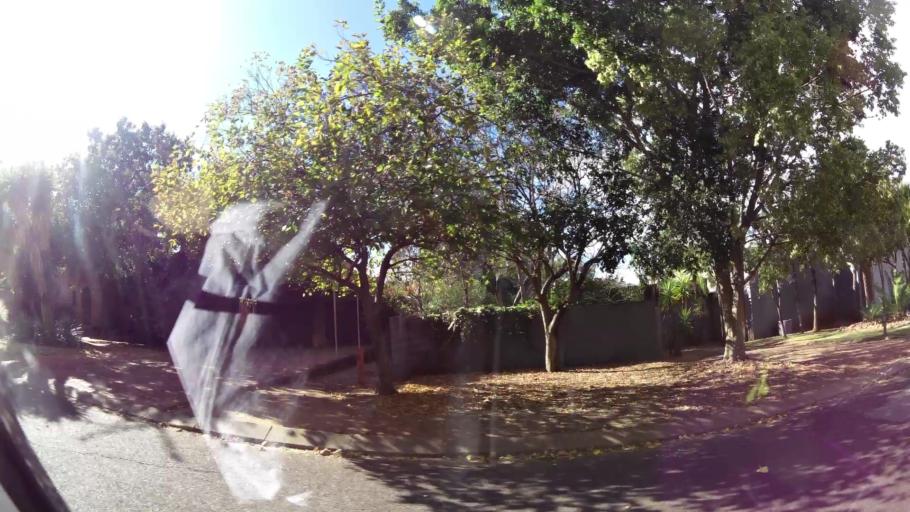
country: ZA
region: Limpopo
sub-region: Waterberg District Municipality
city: Warmbaths
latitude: -24.8730
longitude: 28.2865
